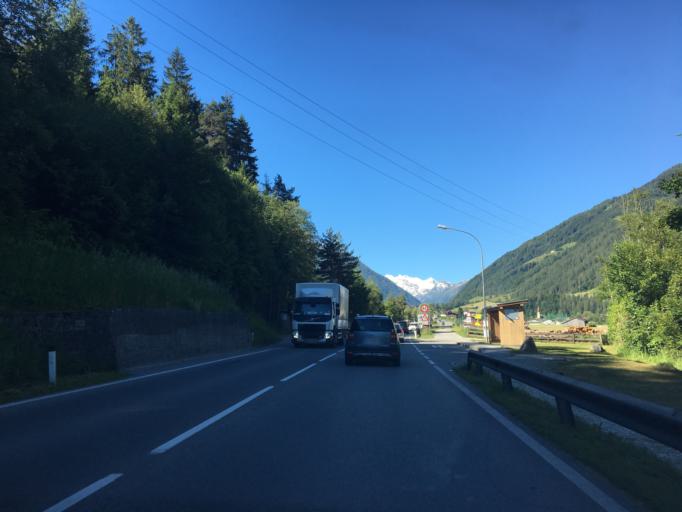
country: AT
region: Tyrol
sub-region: Politischer Bezirk Innsbruck Land
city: Fulpmes
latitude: 47.1480
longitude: 11.3517
